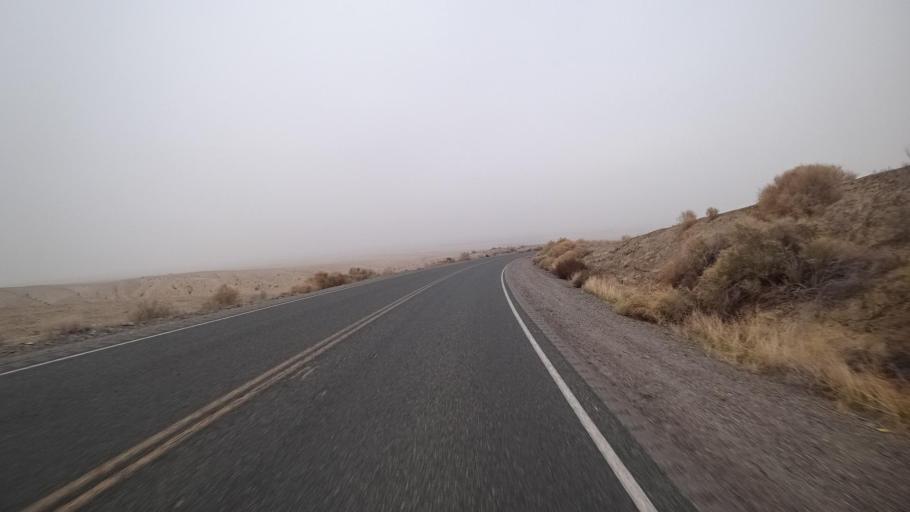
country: US
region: California
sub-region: Kern County
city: Buttonwillow
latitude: 35.3267
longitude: -119.4664
